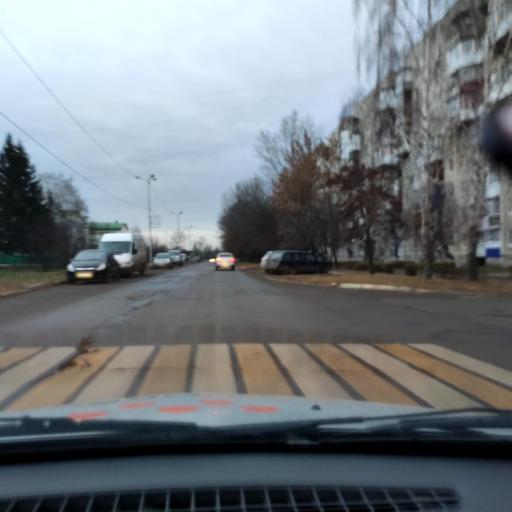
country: RU
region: Bashkortostan
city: Mikhaylovka
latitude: 54.7104
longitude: 55.8273
